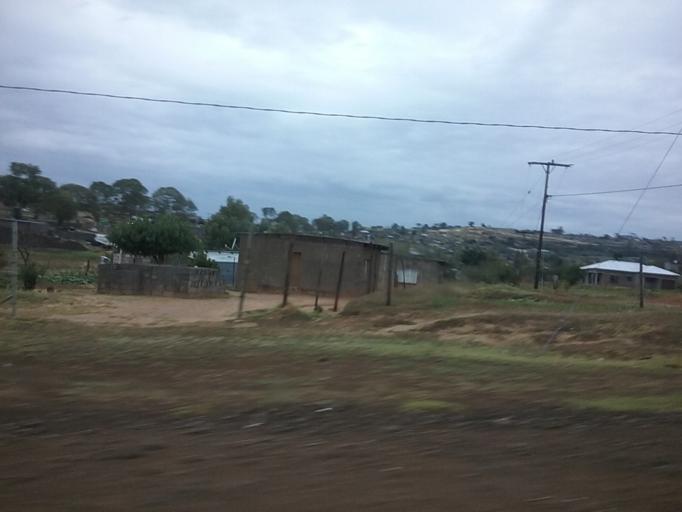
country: LS
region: Berea
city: Teyateyaneng
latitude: -29.1261
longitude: 27.7554
